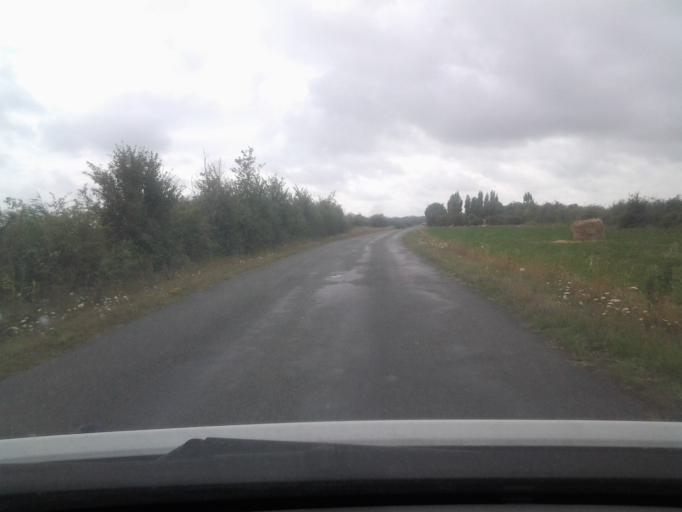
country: FR
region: Pays de la Loire
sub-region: Departement de la Vendee
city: Angles
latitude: 46.3895
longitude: -1.4358
